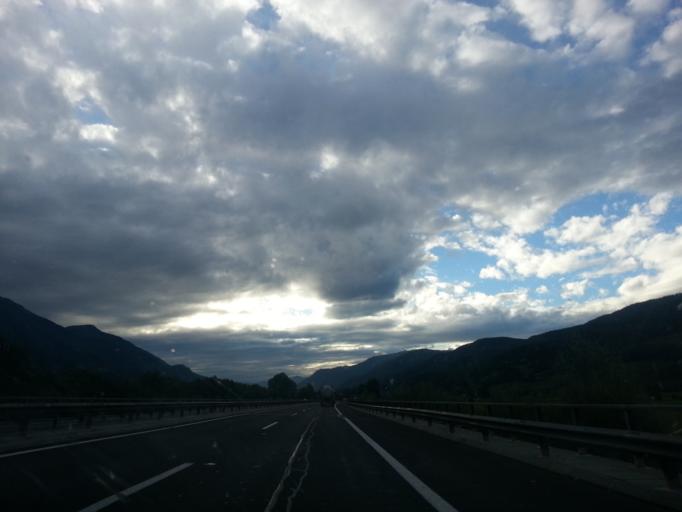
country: AT
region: Styria
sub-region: Politischer Bezirk Liezen
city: Trieben
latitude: 47.4896
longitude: 14.5107
